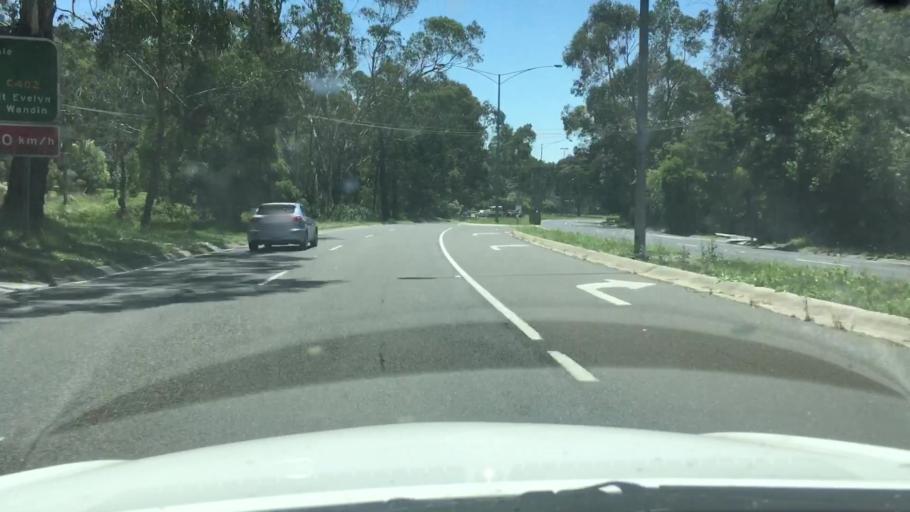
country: AU
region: Victoria
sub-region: Yarra Ranges
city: Kalorama
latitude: -37.7986
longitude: 145.3587
